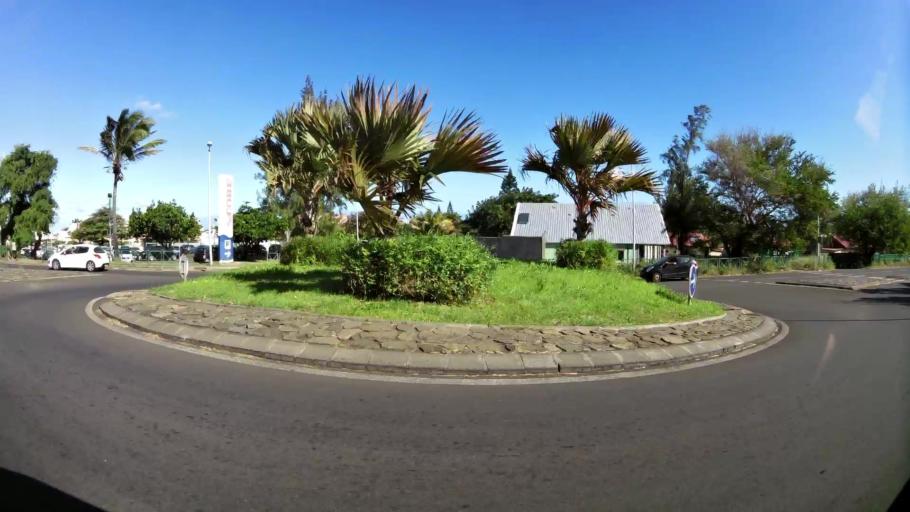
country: RE
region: Reunion
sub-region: Reunion
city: Saint-Pierre
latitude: -21.3472
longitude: 55.4932
